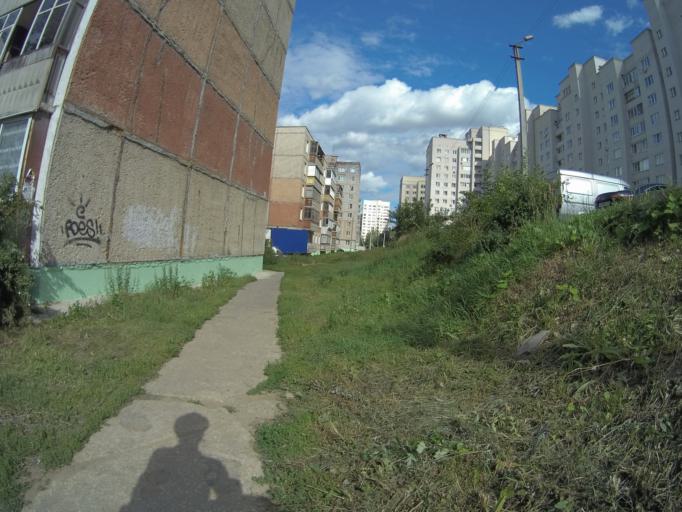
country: RU
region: Vladimir
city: Vladimir
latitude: 56.1196
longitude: 40.3561
